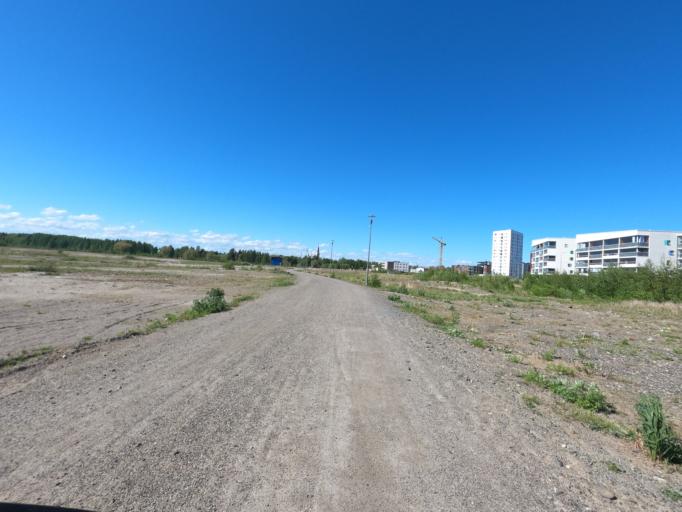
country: FI
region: North Karelia
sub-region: Joensuu
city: Joensuu
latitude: 62.5895
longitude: 29.7594
